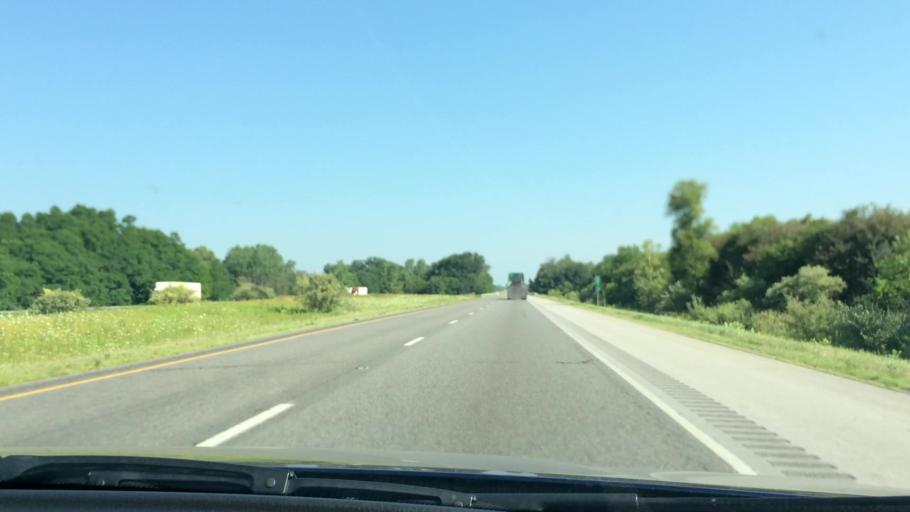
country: US
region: Indiana
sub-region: Jasper County
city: Rensselaer
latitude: 40.8745
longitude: -87.1937
